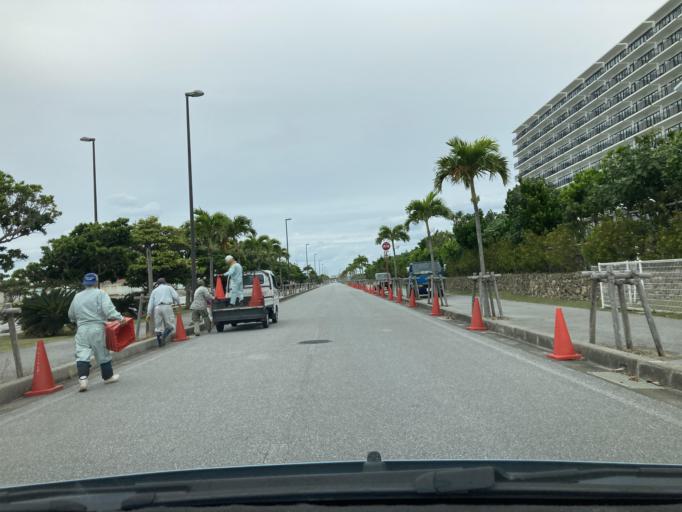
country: JP
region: Okinawa
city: Itoman
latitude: 26.1313
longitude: 127.6525
